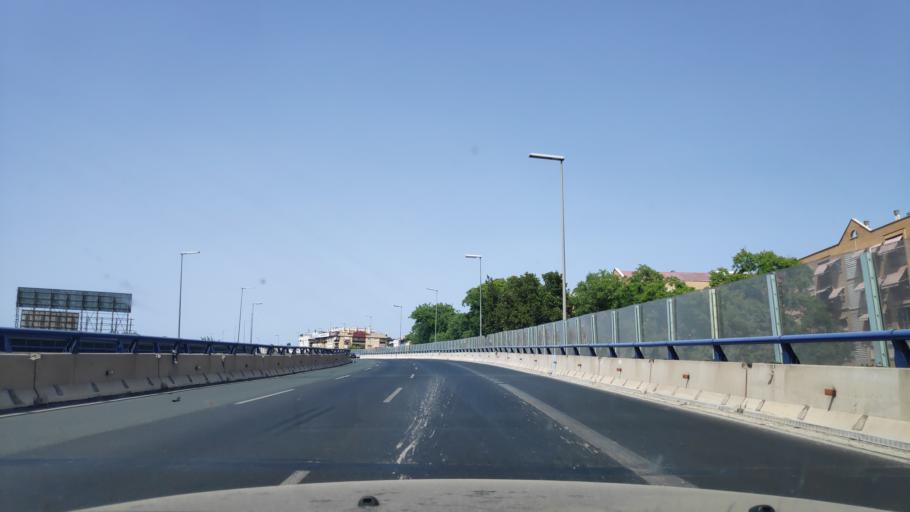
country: ES
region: Murcia
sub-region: Murcia
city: Murcia
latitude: 37.9729
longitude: -1.1372
